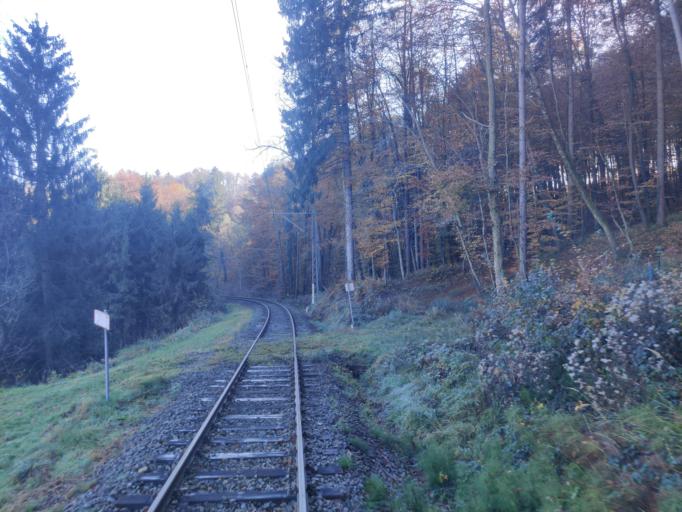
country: AT
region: Styria
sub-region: Politischer Bezirk Suedoststeiermark
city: Gnas
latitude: 46.8803
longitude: 15.8392
